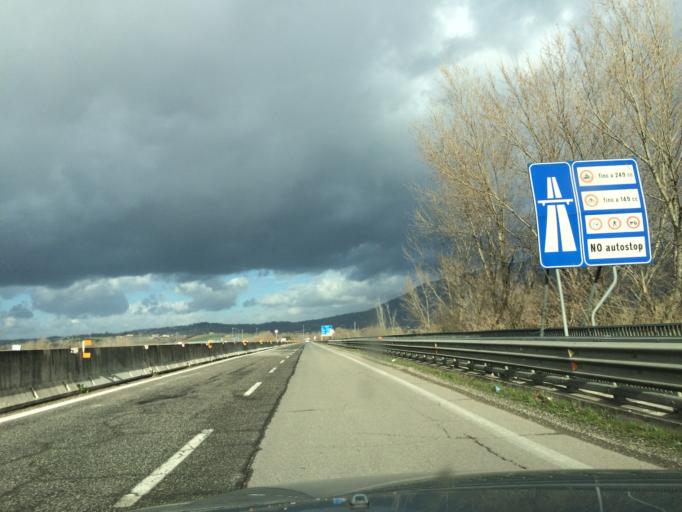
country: IT
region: Umbria
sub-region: Provincia di Terni
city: Terni
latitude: 42.5579
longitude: 12.5829
